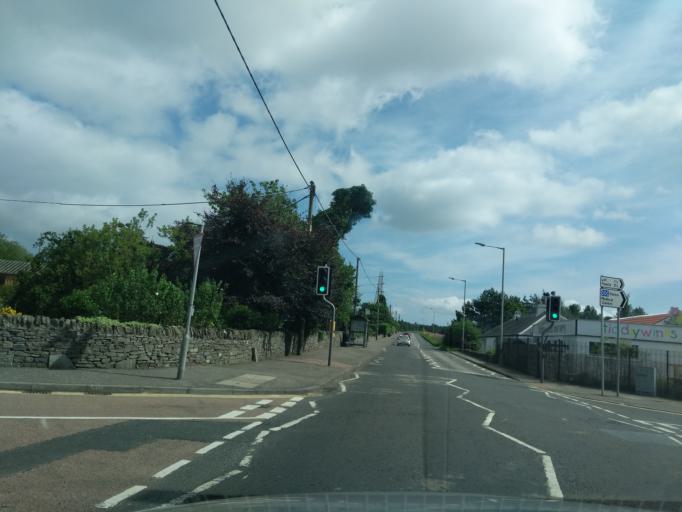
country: GB
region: Scotland
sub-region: Angus
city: Muirhead
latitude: 56.4969
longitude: -3.0666
